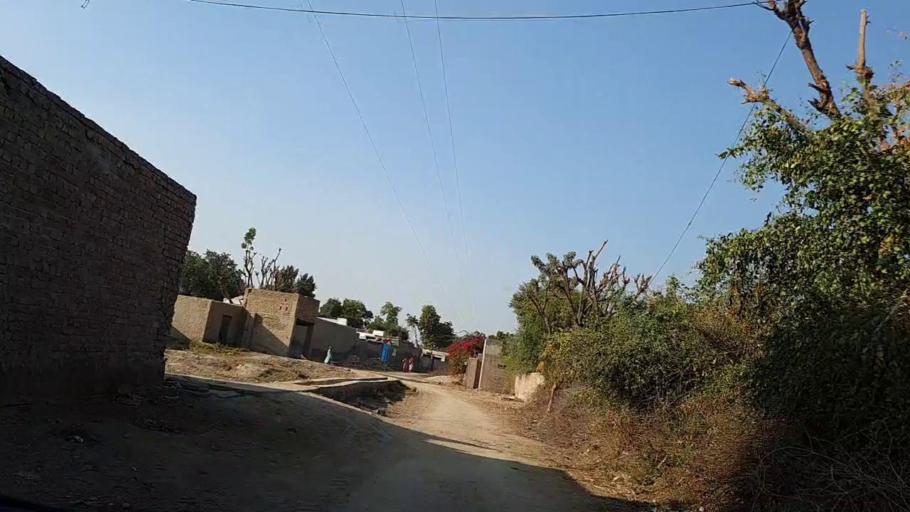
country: PK
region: Sindh
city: Sakrand
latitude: 26.1281
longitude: 68.2218
